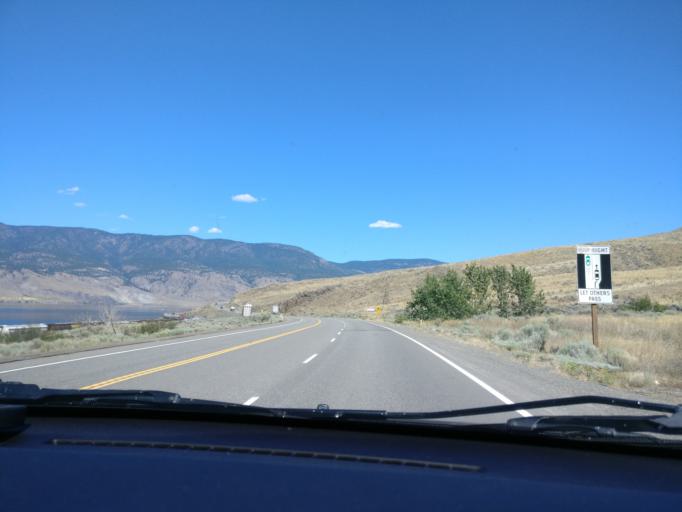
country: CA
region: British Columbia
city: Logan Lake
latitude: 50.7605
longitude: -120.7974
